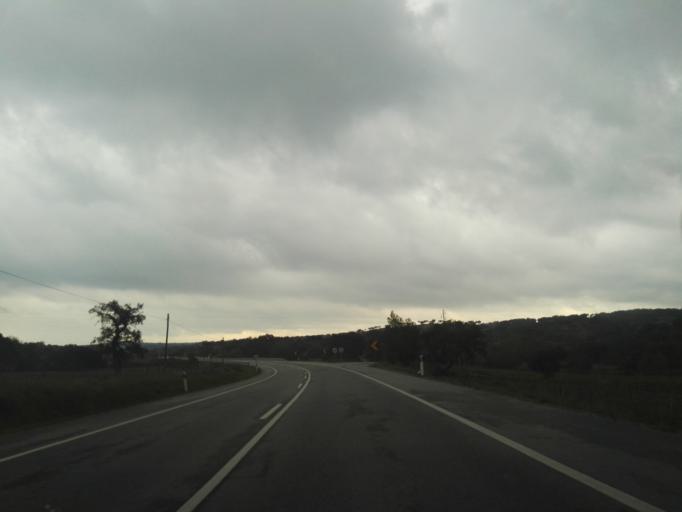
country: PT
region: Portalegre
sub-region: Portalegre
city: Urra
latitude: 39.1984
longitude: -7.3649
